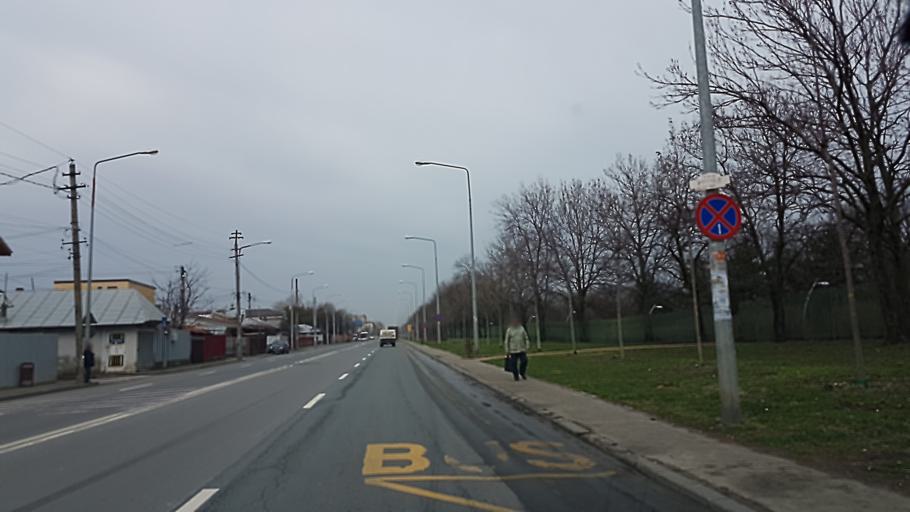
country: RO
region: Ilfov
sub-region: Comuna Pantelimon
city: Pantelimon
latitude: 44.4349
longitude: 26.2038
